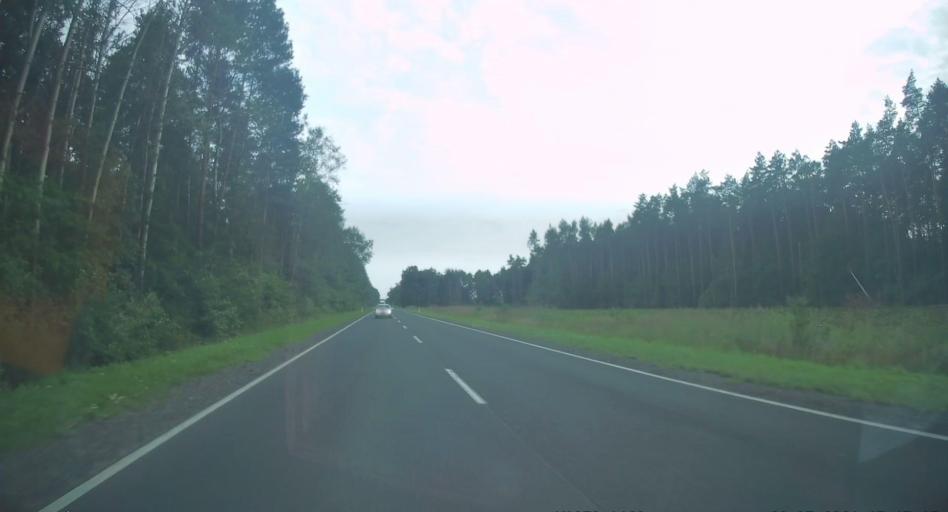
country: PL
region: Lodz Voivodeship
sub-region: Powiat radomszczanski
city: Plawno
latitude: 50.9756
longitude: 19.4094
